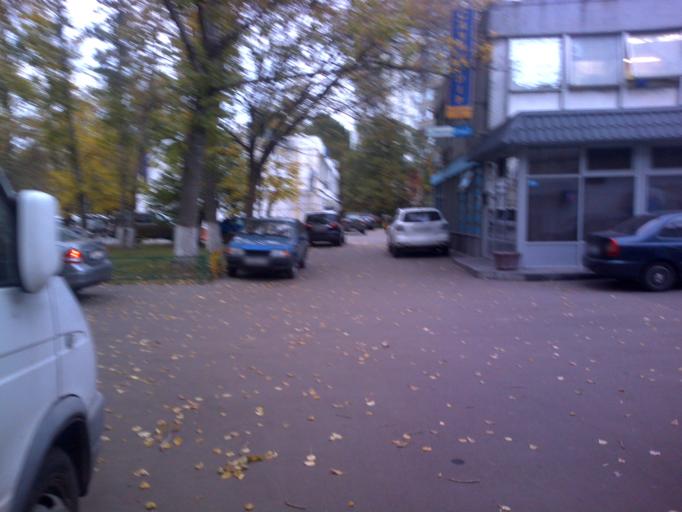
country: RU
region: Moscow
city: Novyye Cheremushki
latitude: 55.6920
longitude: 37.5887
